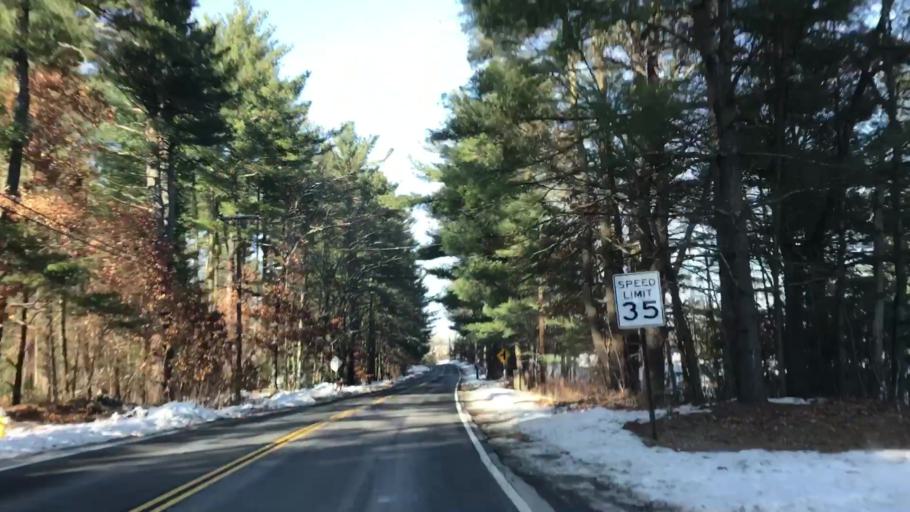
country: US
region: New Hampshire
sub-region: Hillsborough County
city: Milford
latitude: 42.8239
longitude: -71.6067
